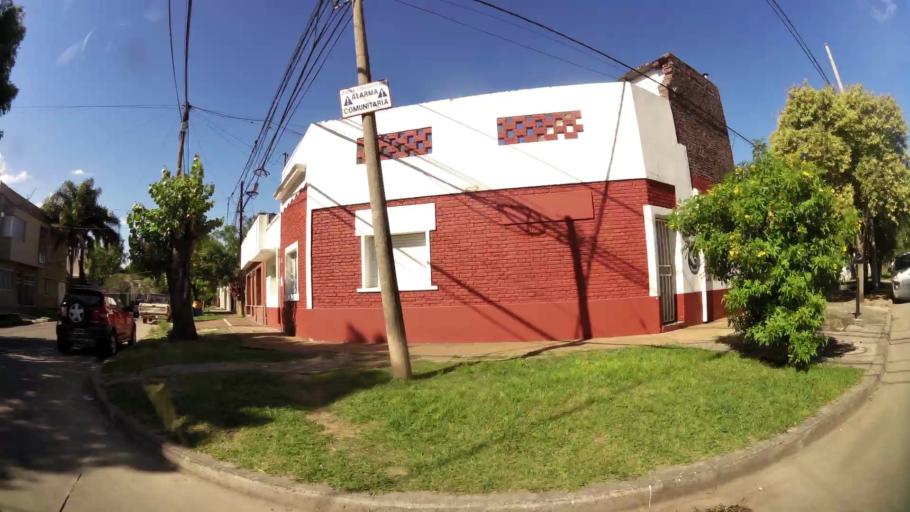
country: AR
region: Santa Fe
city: Santa Fe de la Vera Cruz
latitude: -31.6278
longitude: -60.6938
